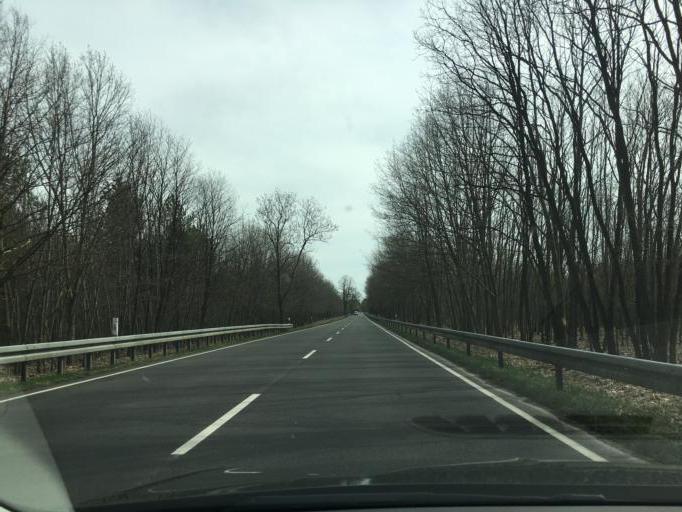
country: DE
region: Brandenburg
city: Spremberg
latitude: 51.5696
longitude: 14.4316
